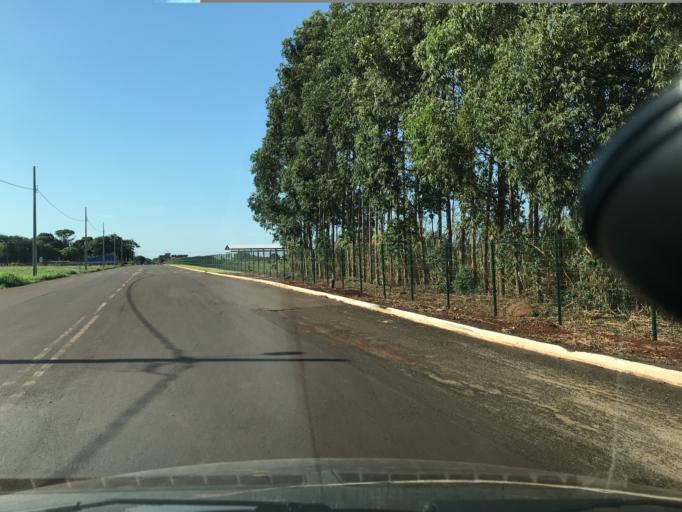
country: BR
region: Parana
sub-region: Palotina
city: Palotina
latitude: -24.2934
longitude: -53.8404
